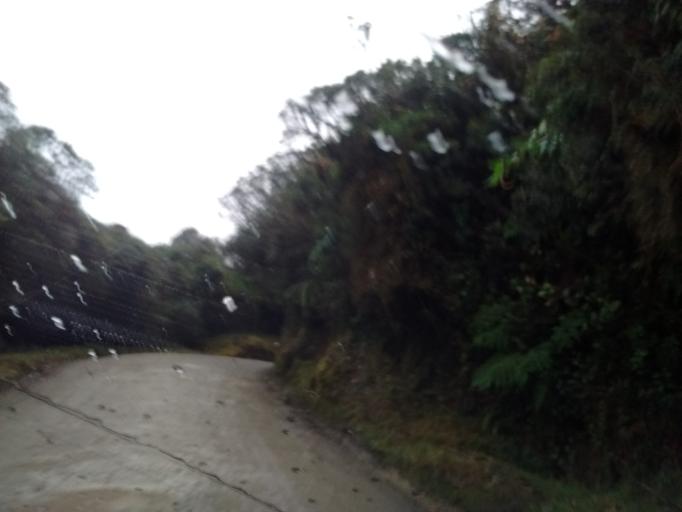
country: CO
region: Cauca
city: Paispamba
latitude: 2.1668
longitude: -76.4102
